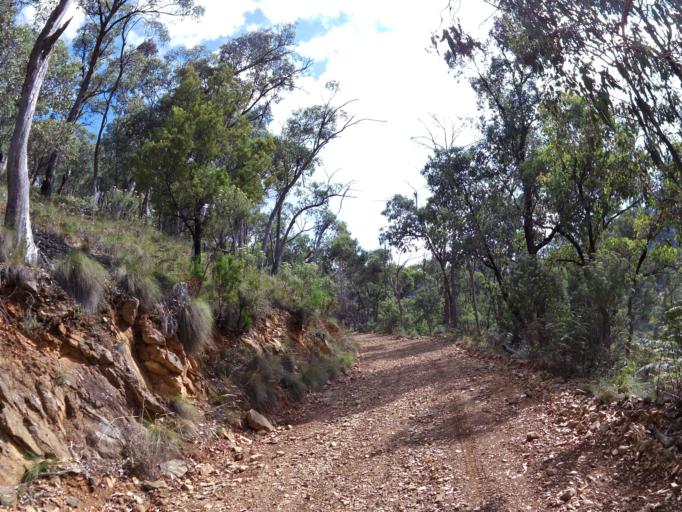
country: AU
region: Victoria
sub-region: Alpine
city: Mount Beauty
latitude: -36.7769
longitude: 147.0143
